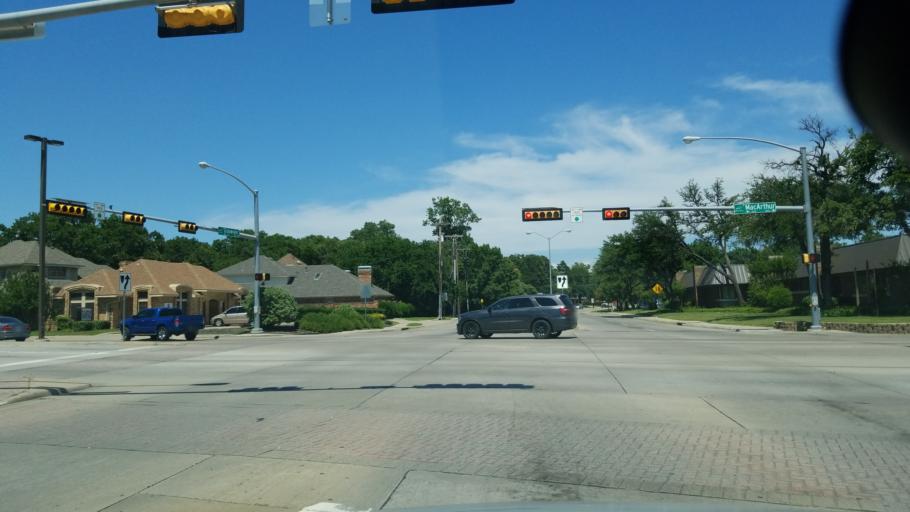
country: US
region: Texas
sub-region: Dallas County
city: Irving
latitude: 32.8290
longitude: -96.9594
